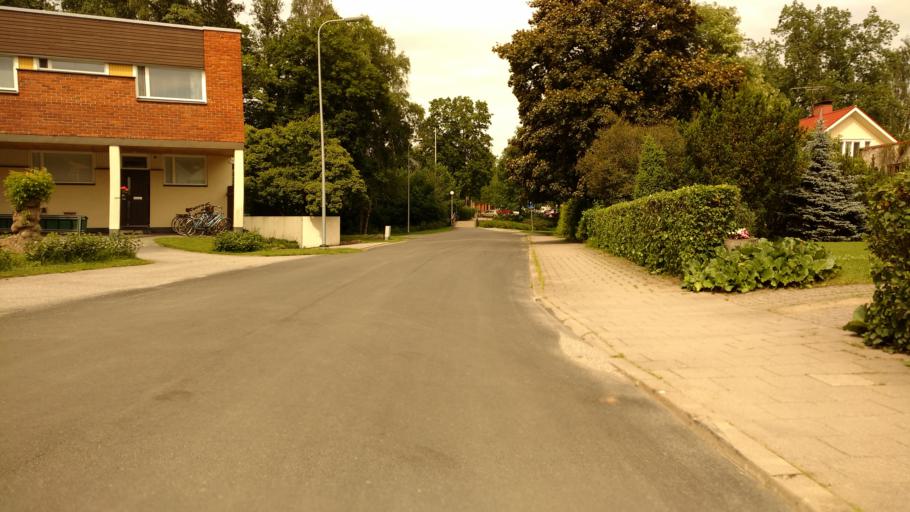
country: FI
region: Varsinais-Suomi
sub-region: Salo
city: Salo
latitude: 60.3821
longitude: 23.1322
